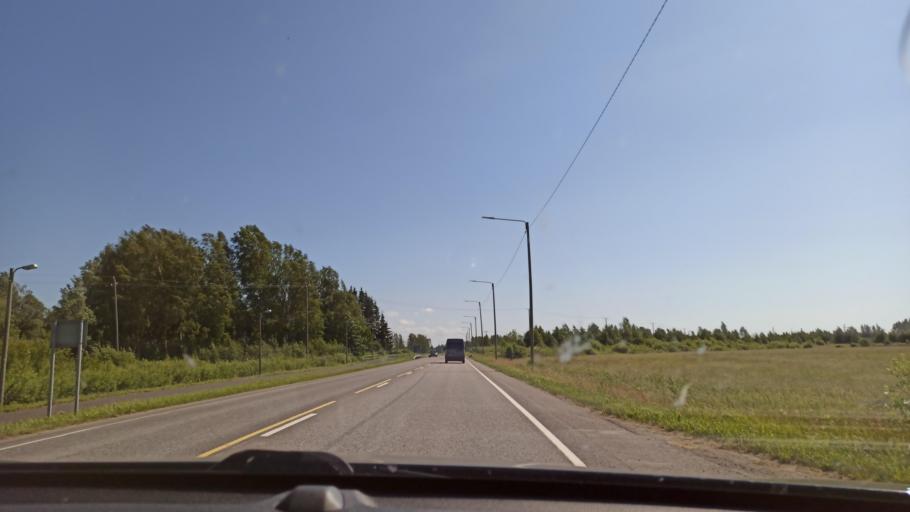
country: FI
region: Satakunta
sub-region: Pori
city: Pori
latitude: 61.5224
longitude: 21.8032
